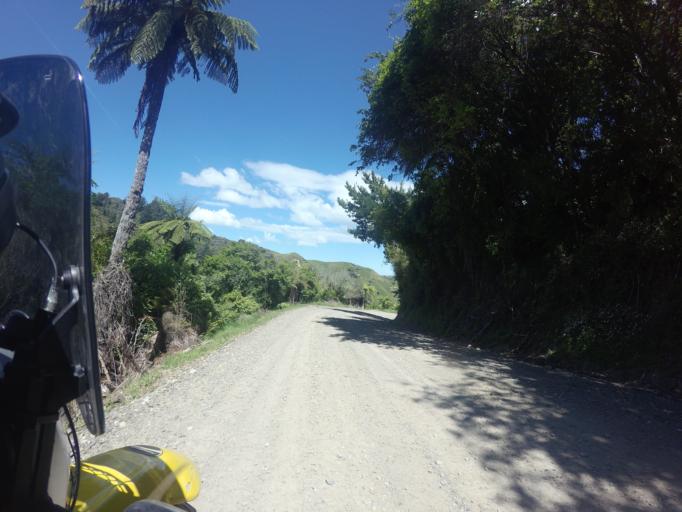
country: NZ
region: Hawke's Bay
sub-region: Wairoa District
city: Wairoa
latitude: -38.9785
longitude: 177.7039
